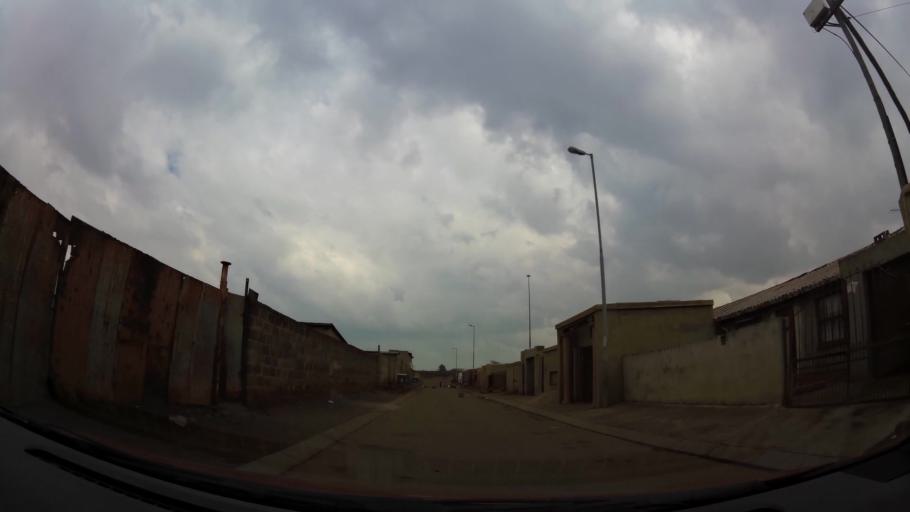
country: ZA
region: Gauteng
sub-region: City of Johannesburg Metropolitan Municipality
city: Soweto
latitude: -26.2585
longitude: 27.8296
